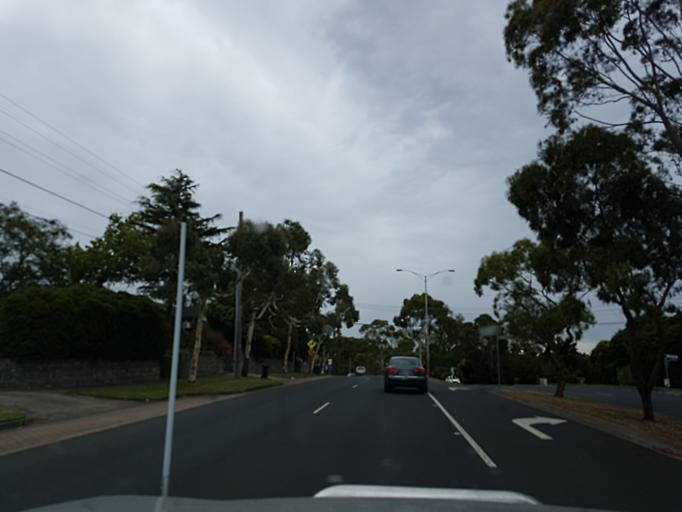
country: AU
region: Victoria
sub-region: Whitehorse
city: Vermont
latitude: -37.8411
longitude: 145.2036
